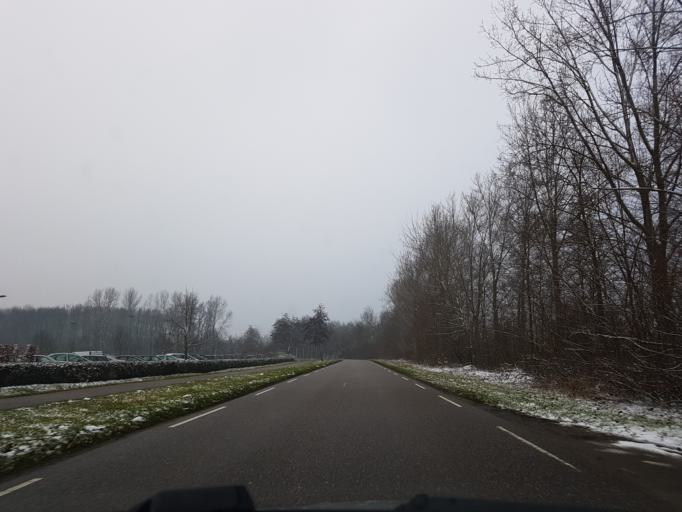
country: NL
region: South Holland
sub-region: Gemeente Lansingerland
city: Bleiswijk
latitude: 51.9954
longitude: 4.5419
